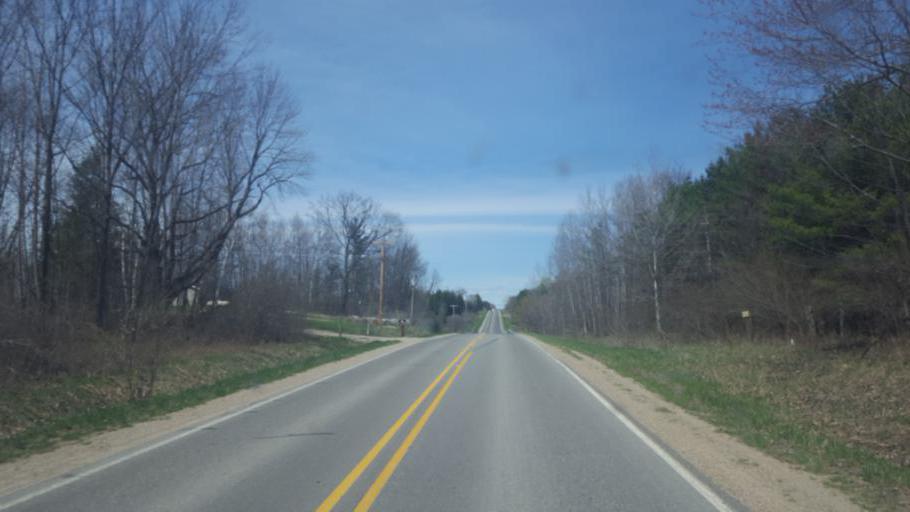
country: US
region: Michigan
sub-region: Gladwin County
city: Gladwin
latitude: 43.9450
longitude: -84.5853
